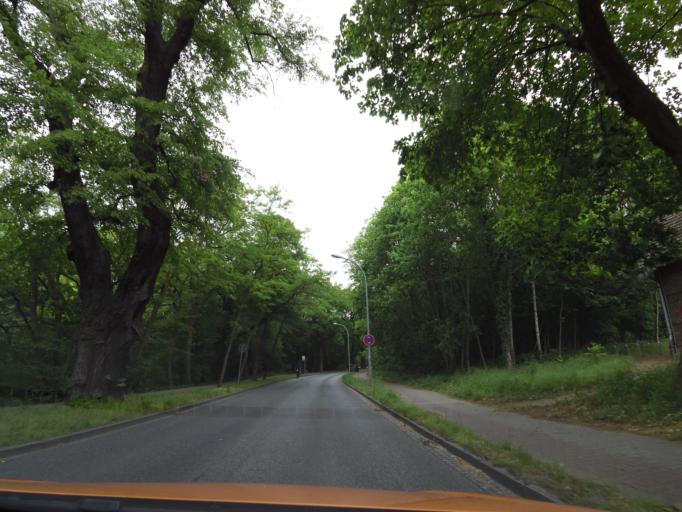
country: DE
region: Brandenburg
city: Kleinmachnow
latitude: 52.3968
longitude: 13.2261
